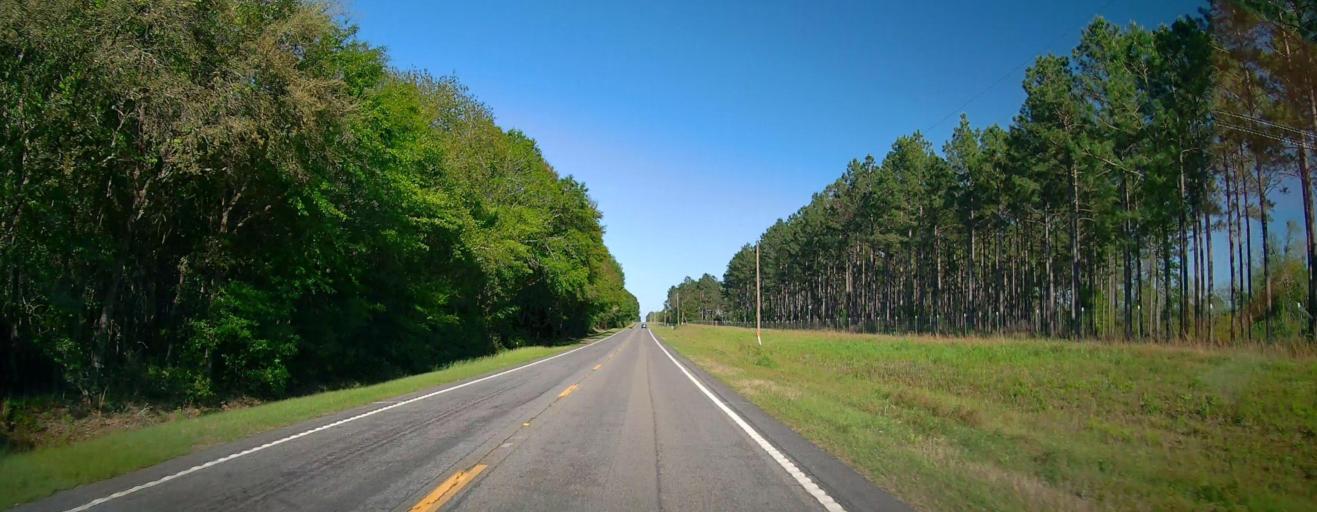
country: US
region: Georgia
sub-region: Ben Hill County
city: Fitzgerald
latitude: 31.7191
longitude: -83.3624
